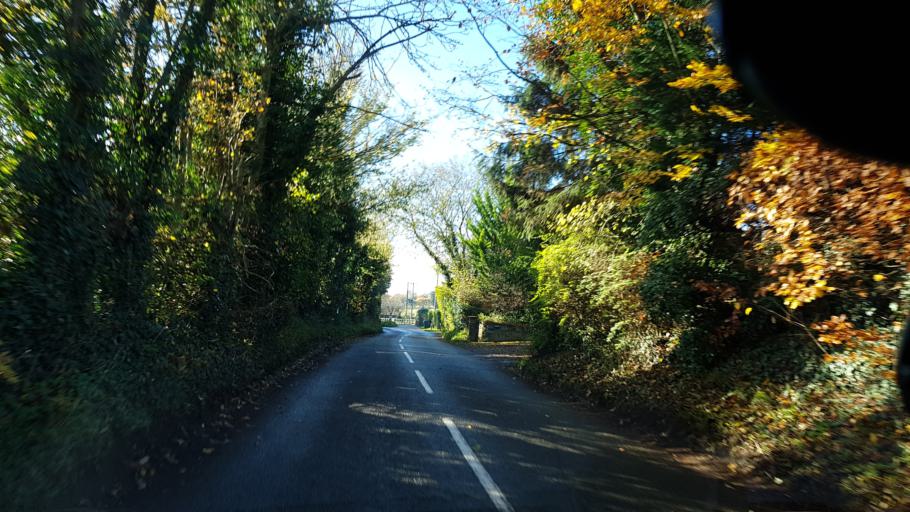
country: GB
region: England
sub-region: Surrey
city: Normandy
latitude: 51.2199
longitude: -0.6695
